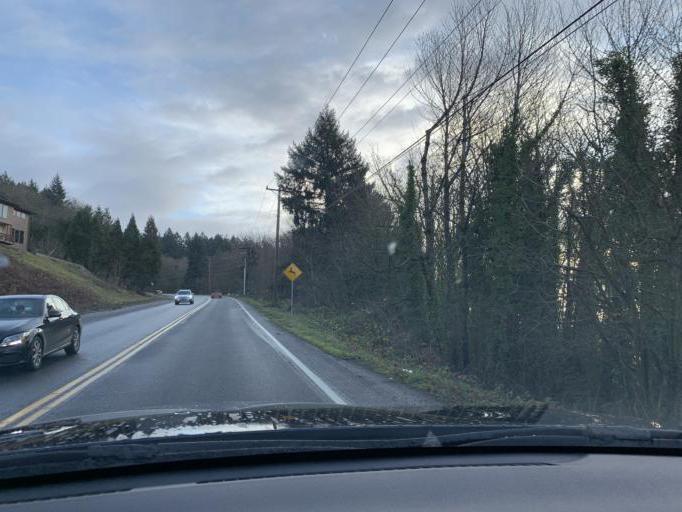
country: US
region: Oregon
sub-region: Multnomah County
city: Fairview
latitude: 45.5845
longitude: -122.4642
